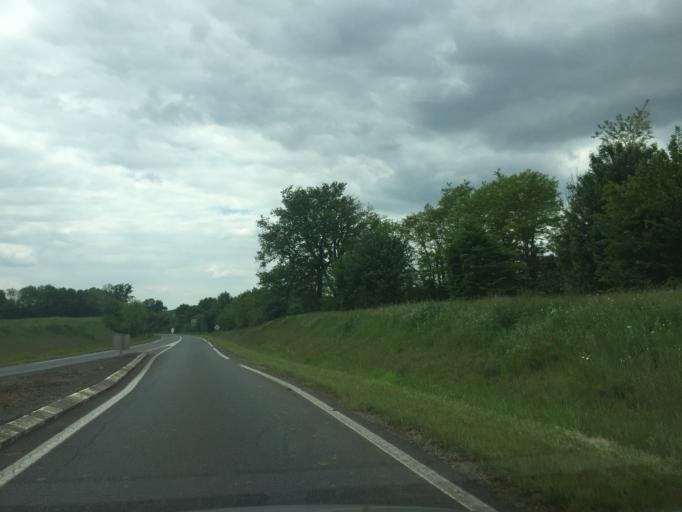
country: FR
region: Poitou-Charentes
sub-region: Departement de la Vienne
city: Lusignan
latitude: 46.4548
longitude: 0.1432
